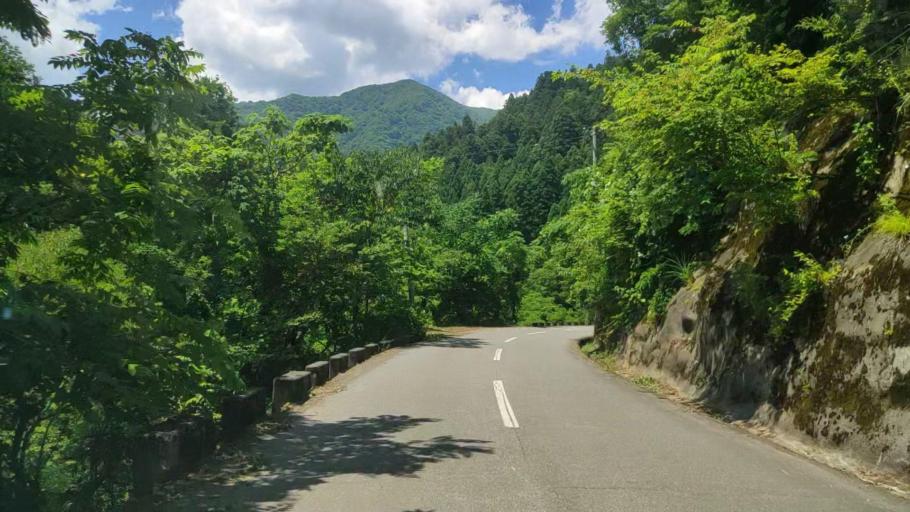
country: JP
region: Fukui
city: Ono
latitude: 35.8744
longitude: 136.5012
